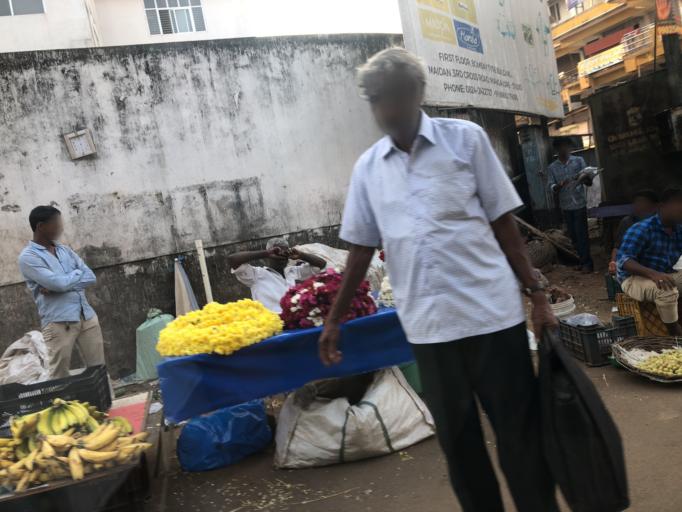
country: IN
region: Karnataka
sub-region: Dakshina Kannada
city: Mangalore
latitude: 12.8656
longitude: 74.8386
